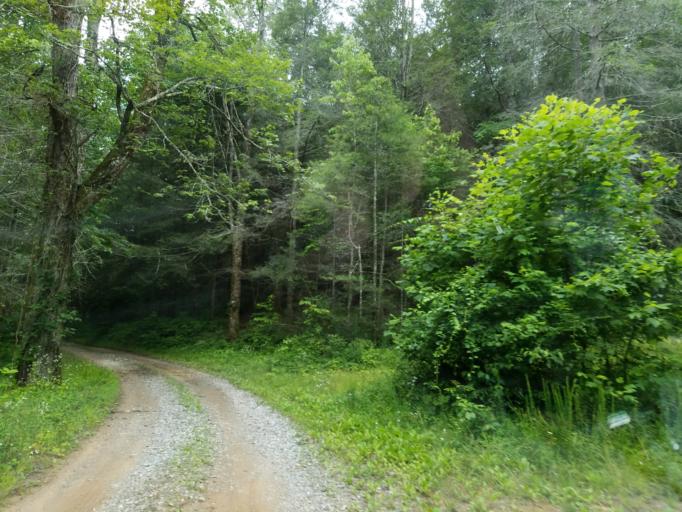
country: US
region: Georgia
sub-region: Union County
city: Blairsville
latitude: 34.7638
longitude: -84.0332
